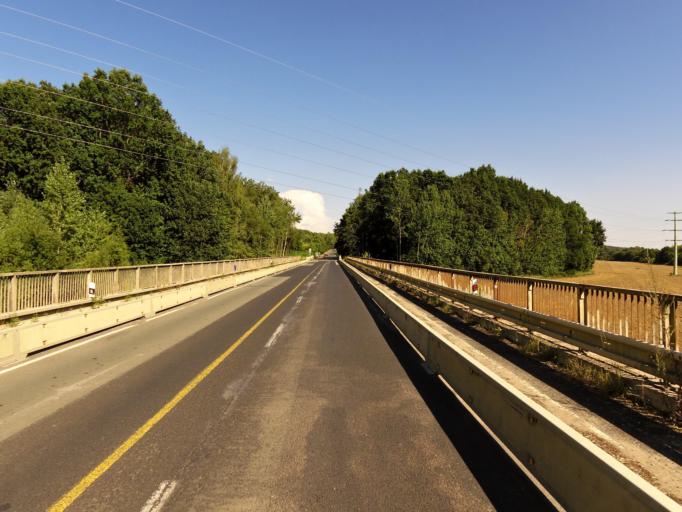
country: CZ
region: Central Bohemia
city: Mnichovo Hradiste
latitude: 50.5192
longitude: 14.9515
